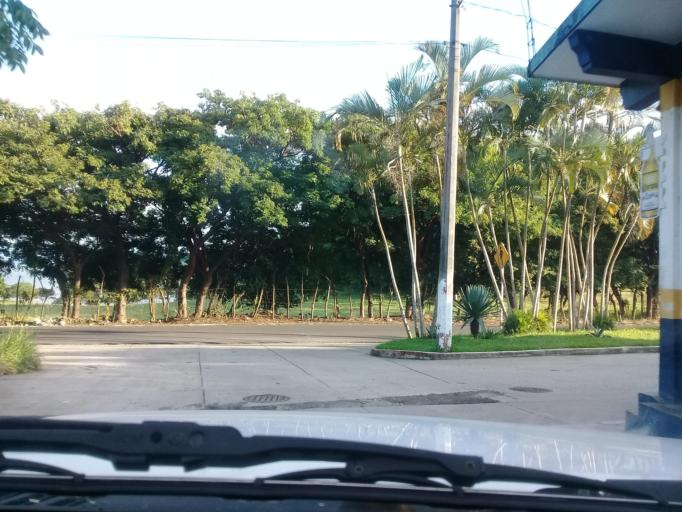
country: MX
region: Veracruz
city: Catemaco
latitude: 18.4232
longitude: -95.0990
